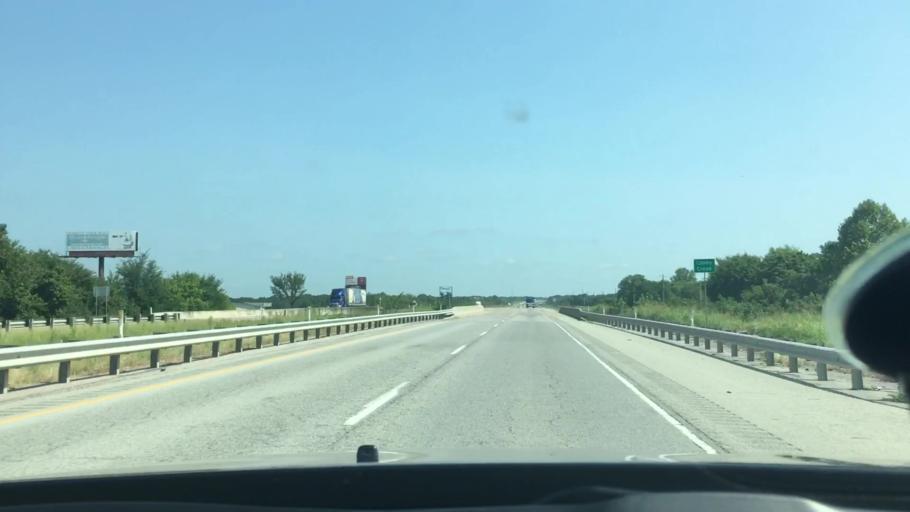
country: US
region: Oklahoma
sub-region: Atoka County
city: Atoka
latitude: 34.2417
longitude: -96.2189
